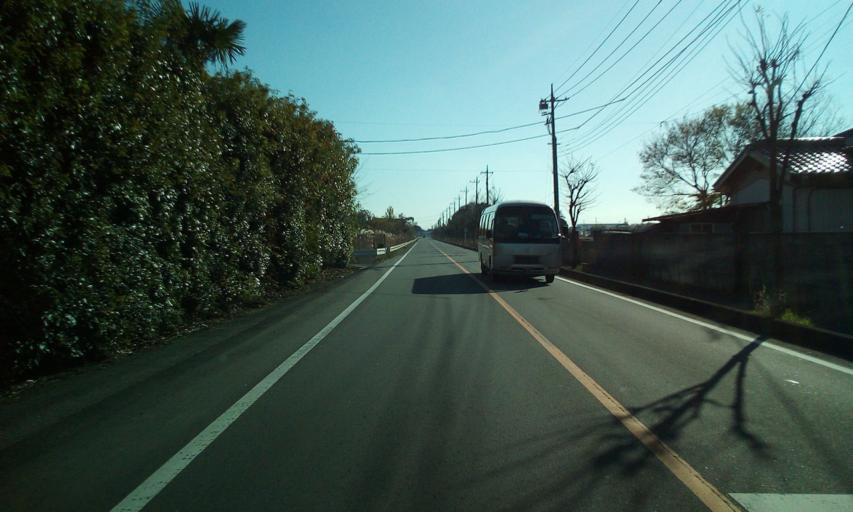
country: JP
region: Saitama
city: Kasukabe
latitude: 36.0030
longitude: 139.7955
